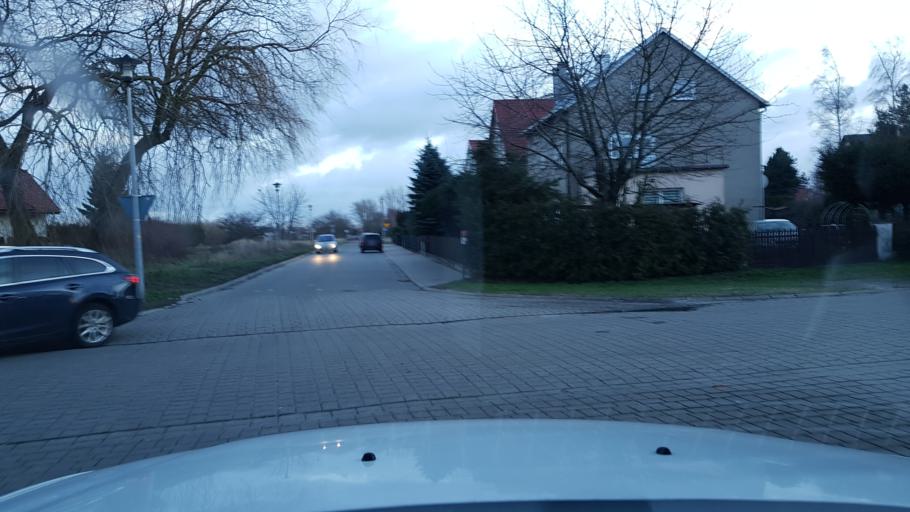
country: PL
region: West Pomeranian Voivodeship
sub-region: Powiat kolobrzeski
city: Kolobrzeg
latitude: 54.1570
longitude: 15.5502
